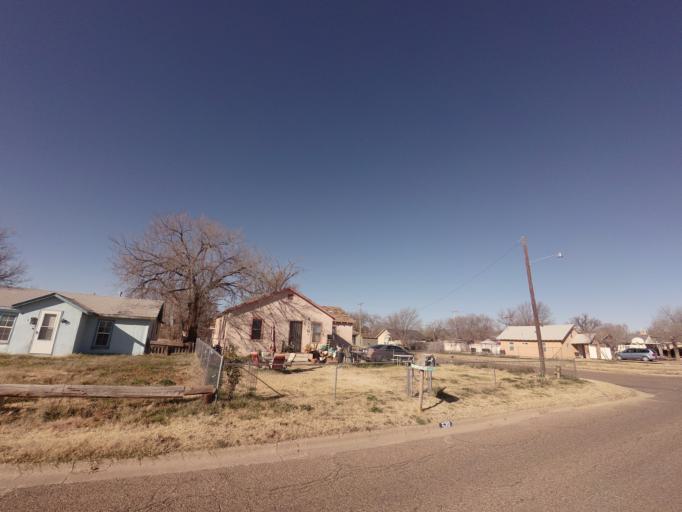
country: US
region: New Mexico
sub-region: Curry County
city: Clovis
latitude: 34.4037
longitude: -103.1940
